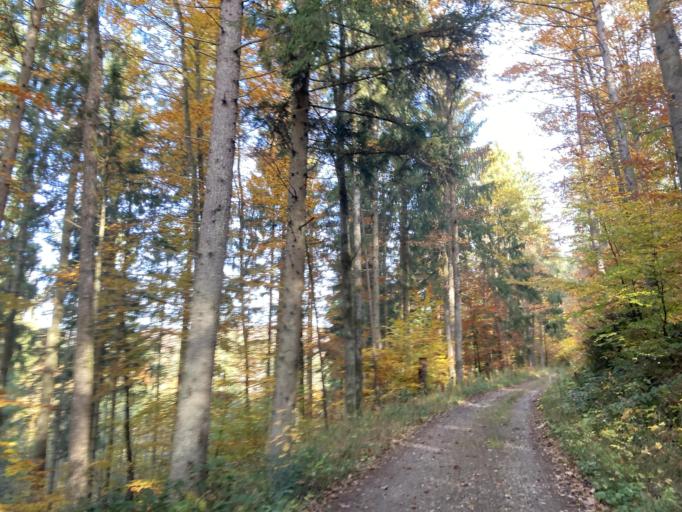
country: DE
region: Baden-Wuerttemberg
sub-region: Tuebingen Region
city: Bodelshausen
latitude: 48.4234
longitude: 8.9624
